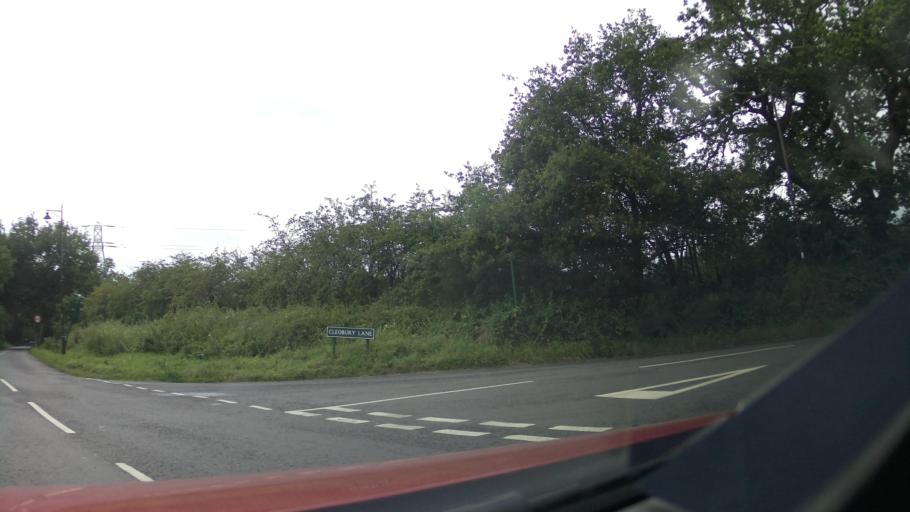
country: GB
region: England
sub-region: Solihull
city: Dickens Heath
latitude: 52.3808
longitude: -1.8418
